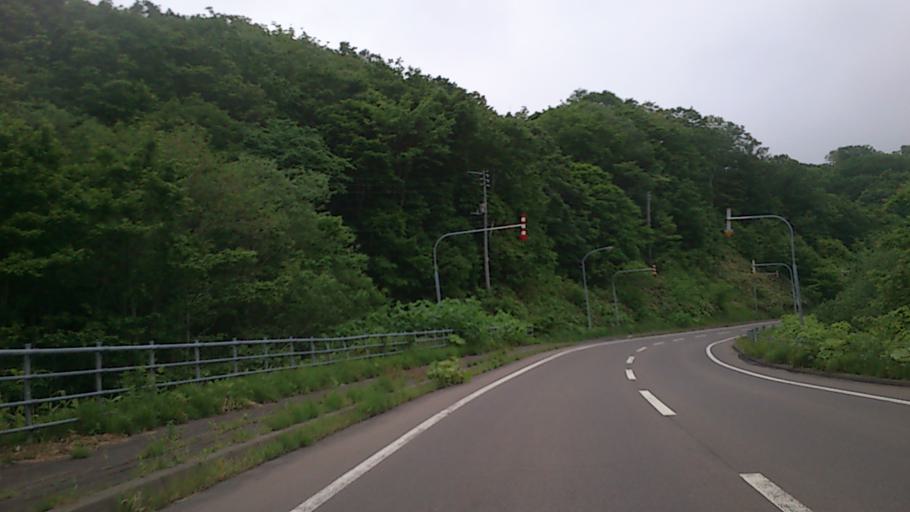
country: JP
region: Hokkaido
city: Iwanai
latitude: 42.8098
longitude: 140.4584
